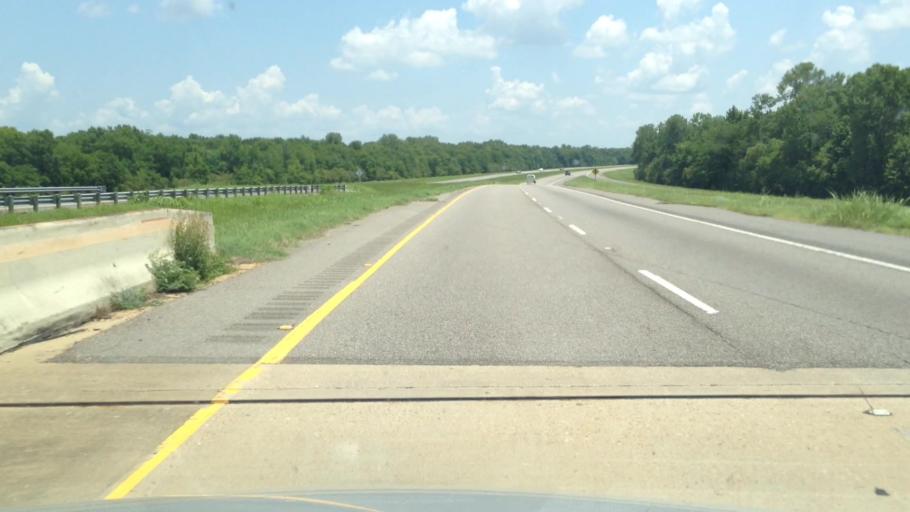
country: US
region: Louisiana
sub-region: Avoyelles Parish
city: Bunkie
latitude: 30.9872
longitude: -92.3078
